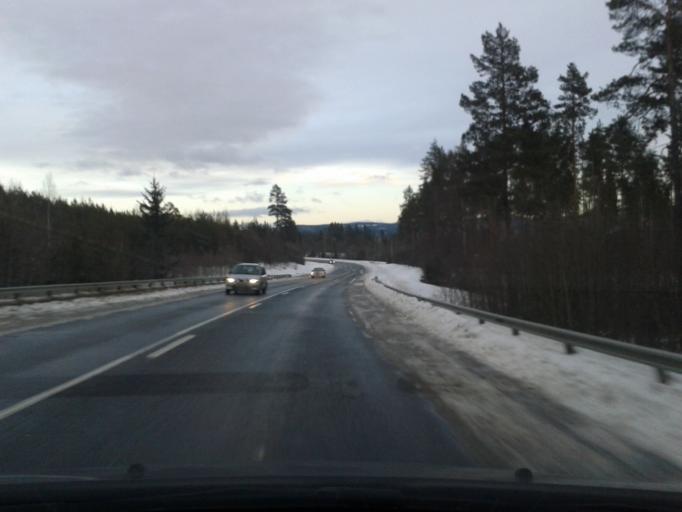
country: SE
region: Vaesternorrland
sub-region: Solleftea Kommun
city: Solleftea
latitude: 63.3333
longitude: 17.1177
